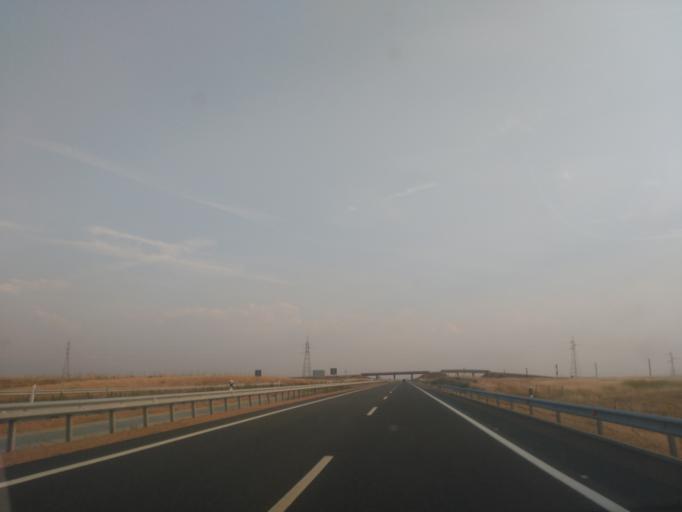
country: ES
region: Castille and Leon
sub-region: Provincia de Zamora
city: Montamarta
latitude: 41.6254
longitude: -5.7885
